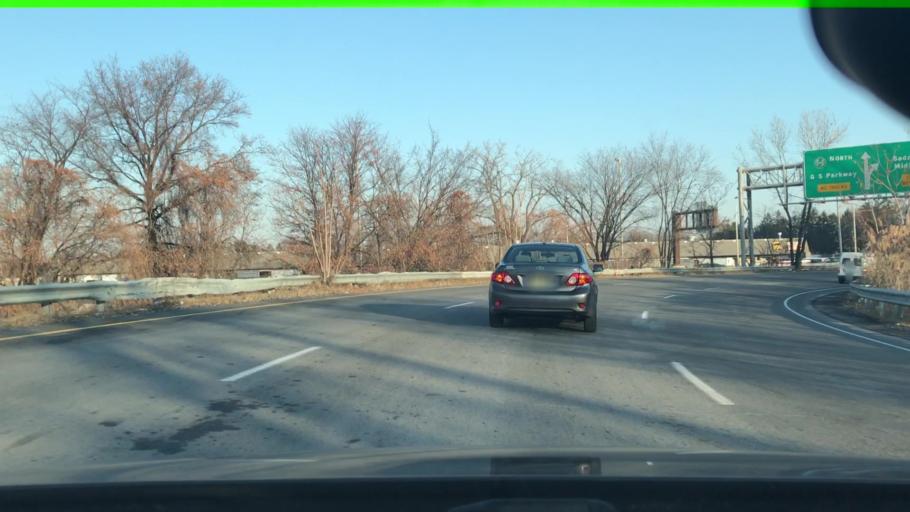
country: US
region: New Jersey
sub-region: Bergen County
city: Saddle Brook
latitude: 40.9065
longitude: -74.1005
